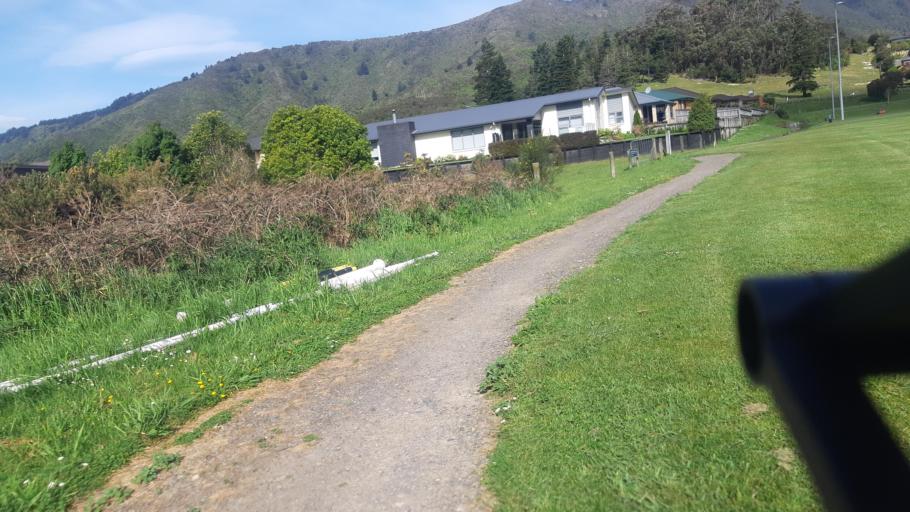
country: NZ
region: Marlborough
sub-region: Marlborough District
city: Picton
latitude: -41.2765
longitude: 174.0245
